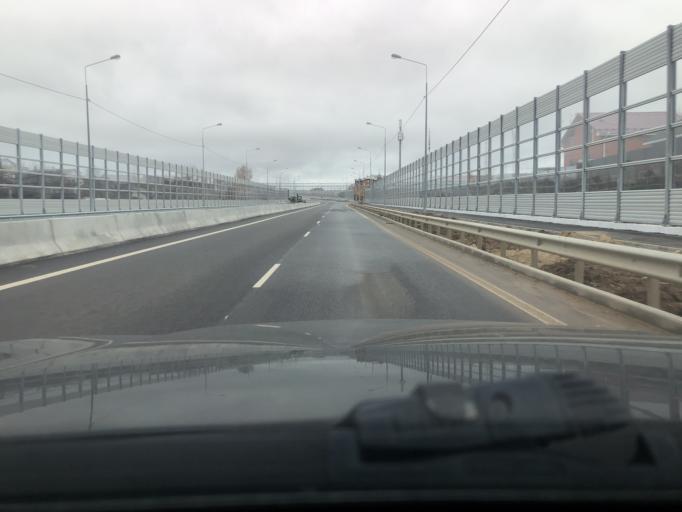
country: RU
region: Moskovskaya
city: Sergiyev Posad
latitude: 56.3049
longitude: 38.1010
